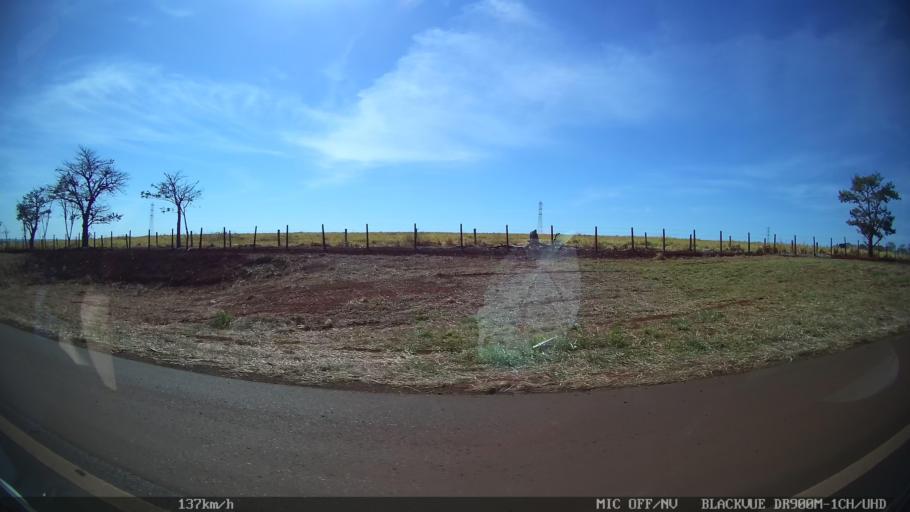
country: BR
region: Sao Paulo
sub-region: Ipua
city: Ipua
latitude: -20.4730
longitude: -48.1021
